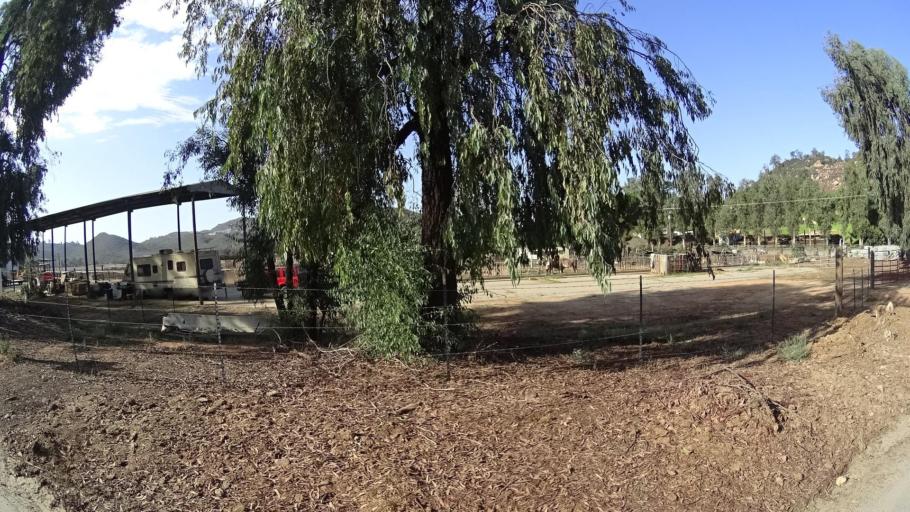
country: US
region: California
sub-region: San Diego County
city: San Pasqual
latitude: 33.1673
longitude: -116.9658
